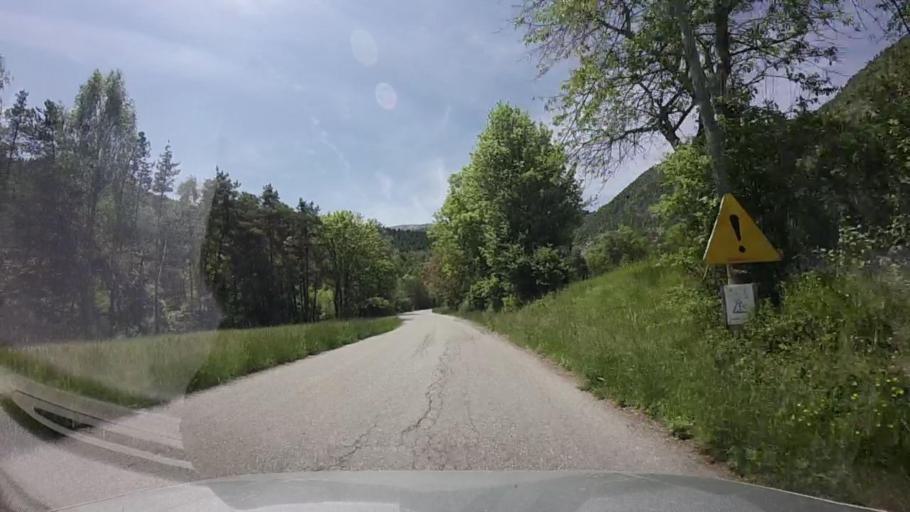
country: FR
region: Provence-Alpes-Cote d'Azur
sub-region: Departement des Alpes-de-Haute-Provence
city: Seyne-les-Alpes
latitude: 44.3624
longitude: 6.2986
